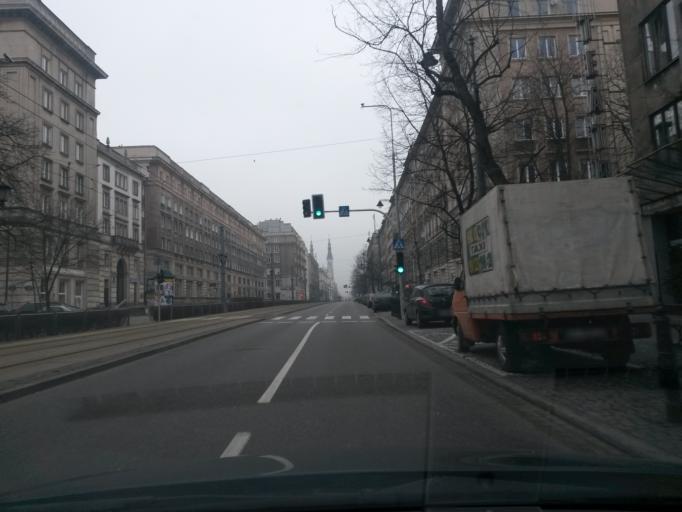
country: PL
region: Masovian Voivodeship
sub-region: Warszawa
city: Srodmiescie
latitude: 52.2149
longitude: 21.0209
